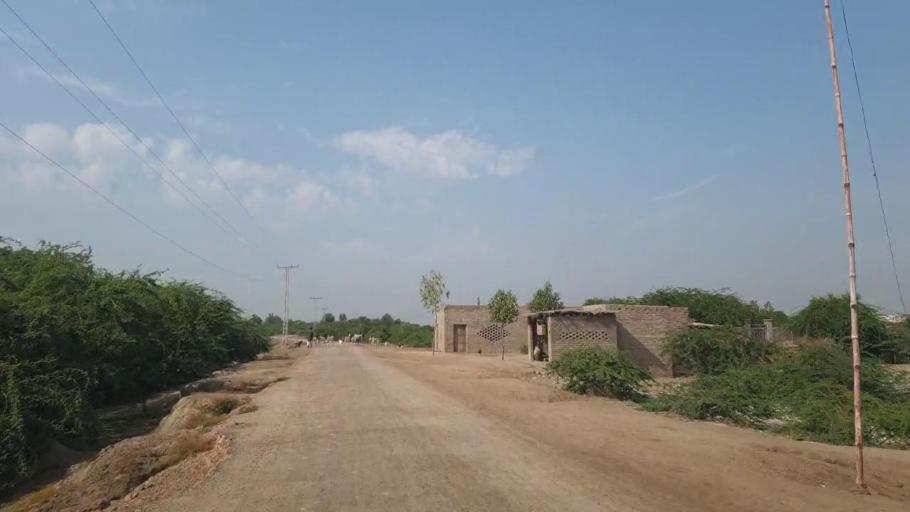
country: PK
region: Sindh
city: Digri
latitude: 25.0068
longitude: 69.0648
